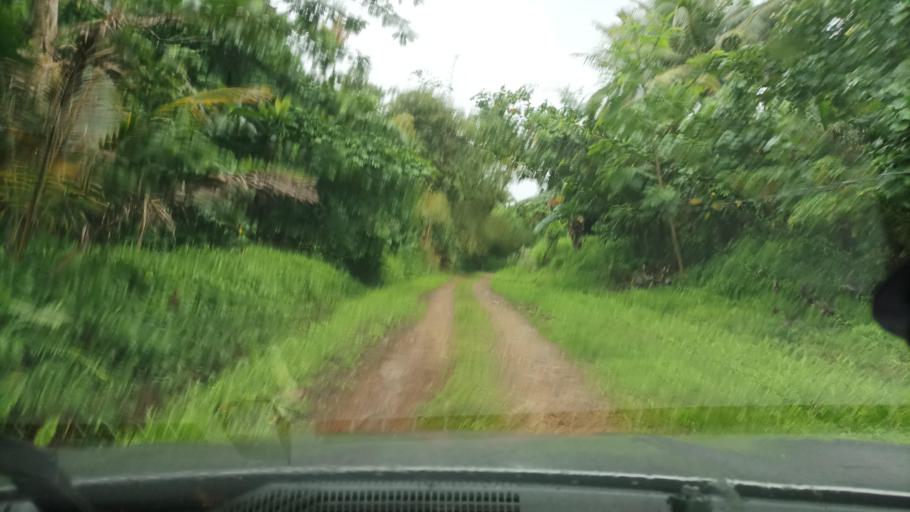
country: FM
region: Pohnpei
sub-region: Sokehs Municipality
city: Palikir - National Government Center
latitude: 6.8553
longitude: 158.1852
